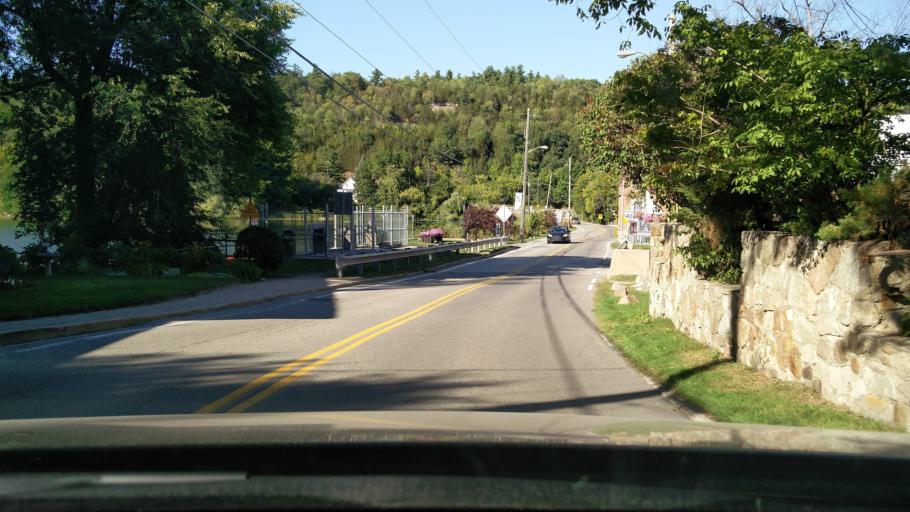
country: CA
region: Ontario
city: Perth
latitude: 44.6799
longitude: -76.3949
